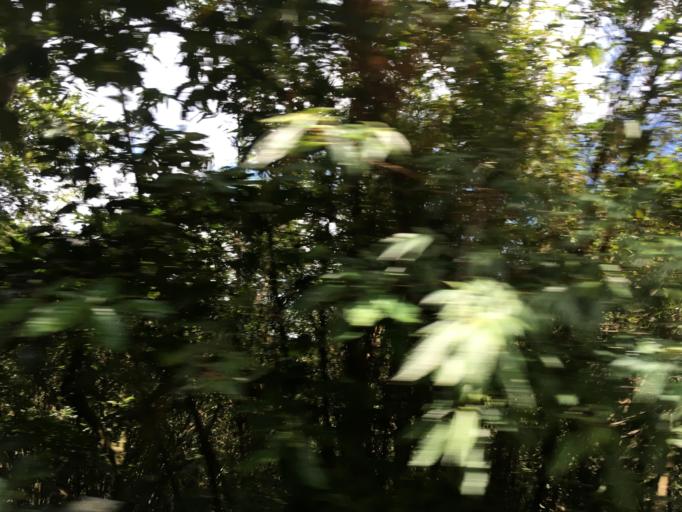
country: TW
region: Taipei
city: Taipei
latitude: 24.9399
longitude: 121.5770
